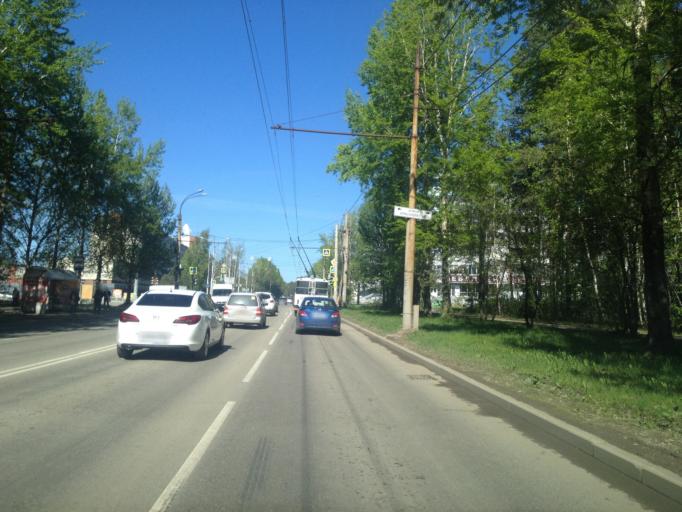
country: RU
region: Sverdlovsk
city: Sovkhoznyy
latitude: 56.7757
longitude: 60.5508
